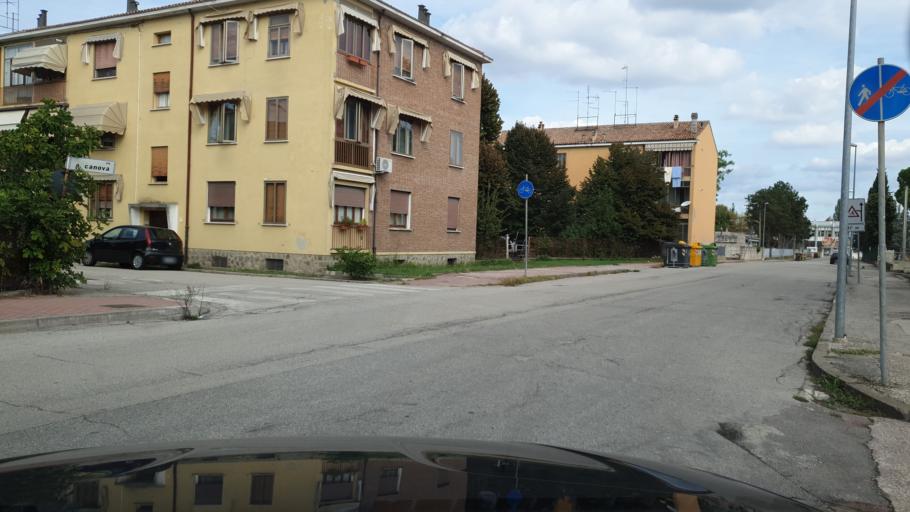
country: IT
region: Veneto
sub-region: Provincia di Rovigo
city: Rovigo
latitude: 45.0794
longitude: 11.7925
